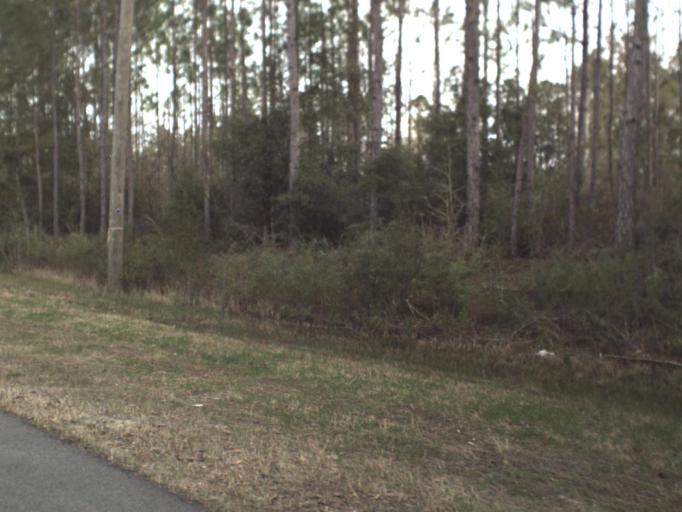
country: US
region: Florida
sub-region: Bay County
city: Callaway
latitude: 30.1527
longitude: -85.5231
